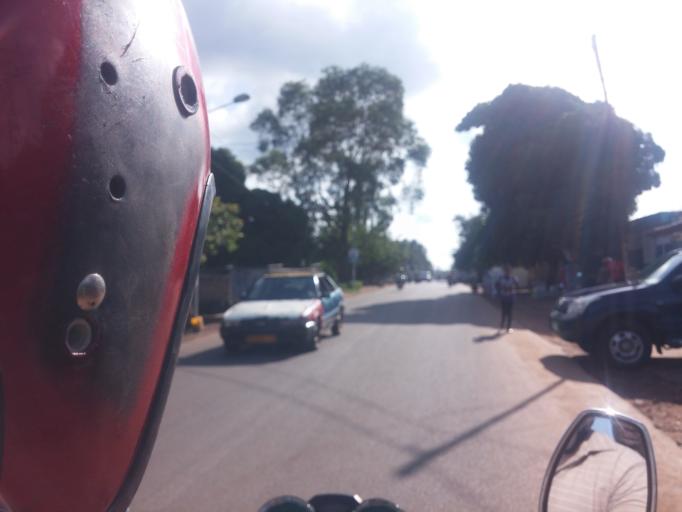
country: TG
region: Kara
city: Kara
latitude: 9.5537
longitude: 1.2053
